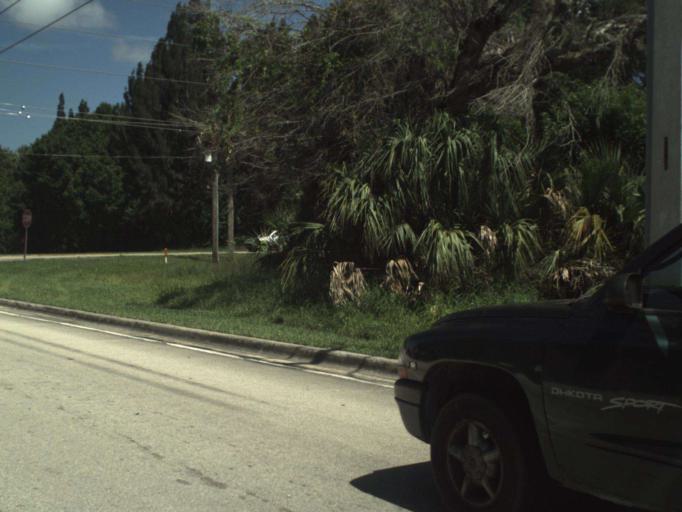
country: US
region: Florida
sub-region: Indian River County
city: Winter Beach
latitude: 27.7485
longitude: -80.4625
